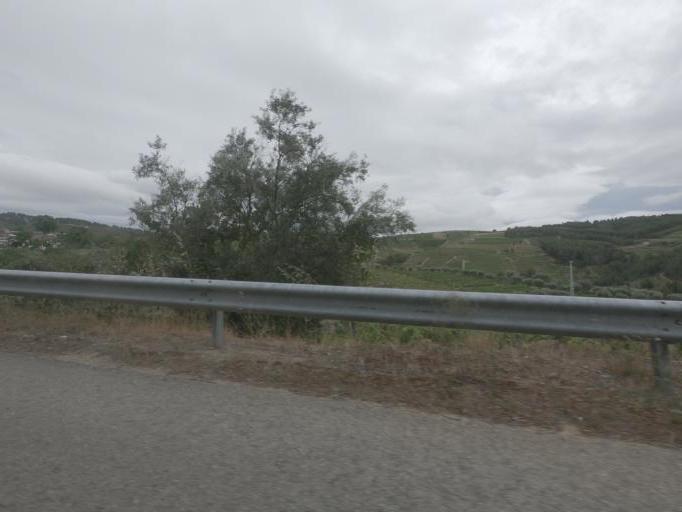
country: PT
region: Vila Real
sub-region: Sabrosa
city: Sabrosa
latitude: 41.2842
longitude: -7.5297
